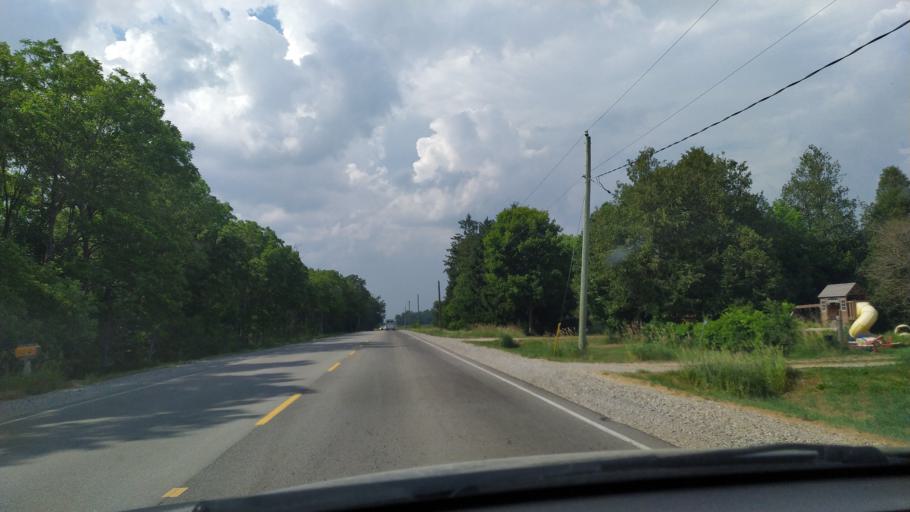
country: CA
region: Ontario
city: Dorchester
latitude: 43.0641
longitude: -81.1375
